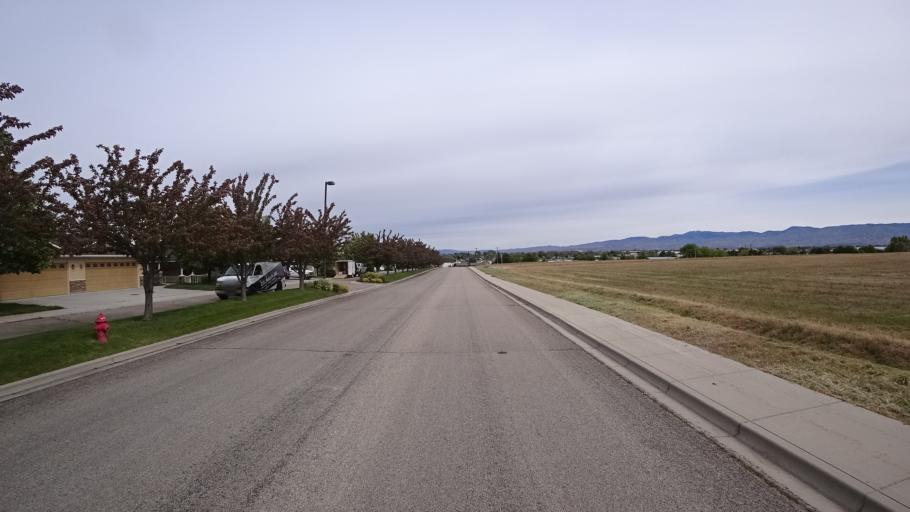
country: US
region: Idaho
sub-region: Ada County
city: Garden City
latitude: 43.5734
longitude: -116.2867
